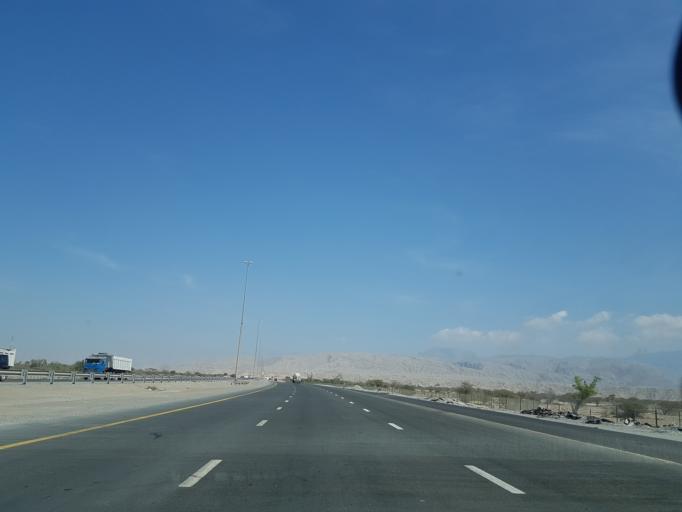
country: AE
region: Ra's al Khaymah
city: Ras al-Khaimah
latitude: 25.7016
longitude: 55.9924
